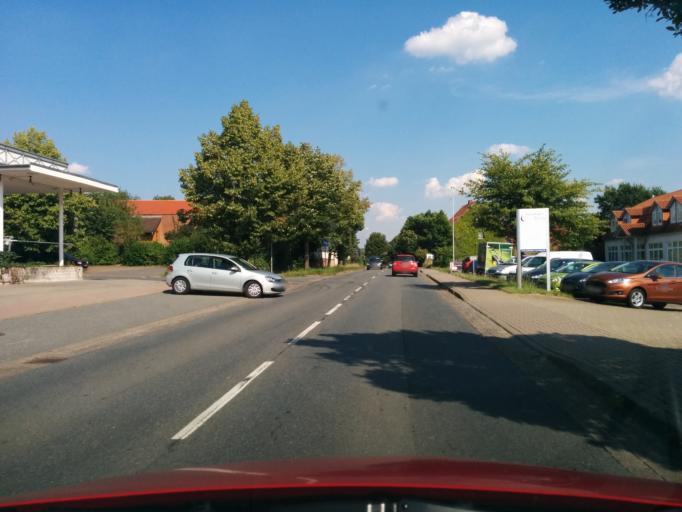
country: DE
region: Lower Saxony
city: Gieboldehausen
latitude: 51.6153
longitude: 10.2190
